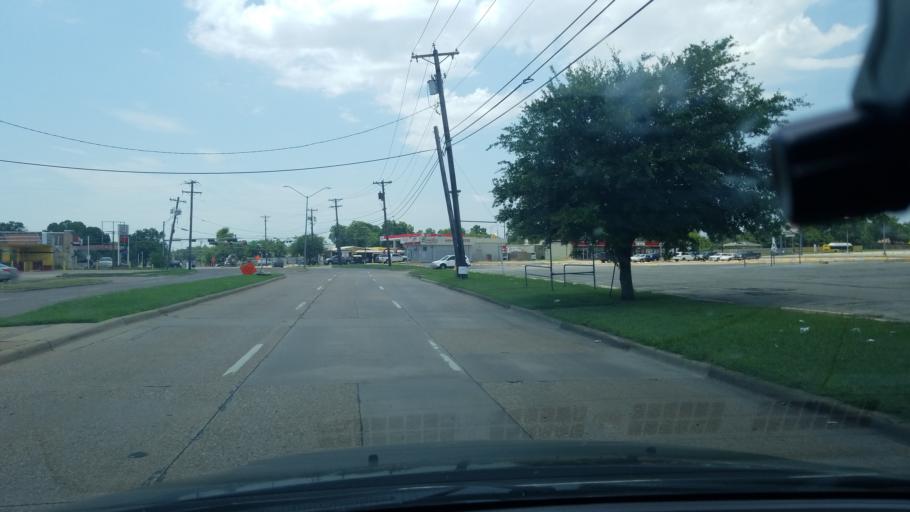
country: US
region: Texas
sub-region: Dallas County
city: Balch Springs
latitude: 32.7503
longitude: -96.6653
